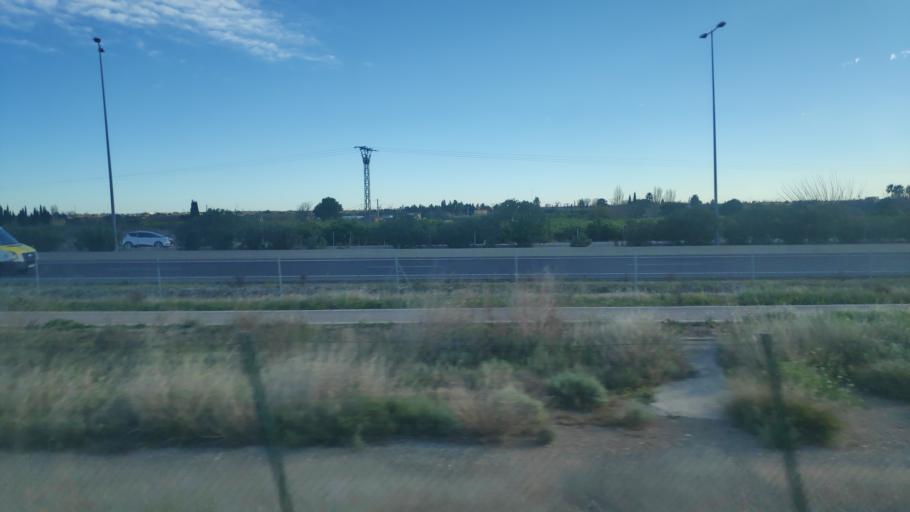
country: ES
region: Valencia
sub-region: Provincia de Castello
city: Castello de la Plana
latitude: 40.0183
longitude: -0.0153
